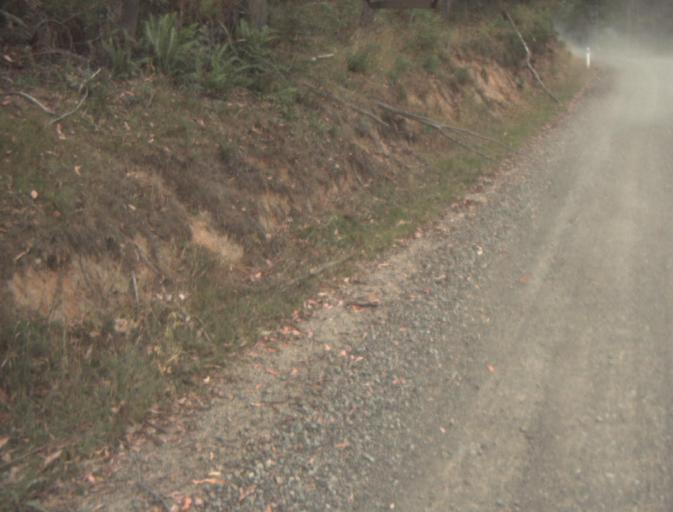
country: AU
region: Tasmania
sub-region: Dorset
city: Scottsdale
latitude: -41.4145
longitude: 147.5206
